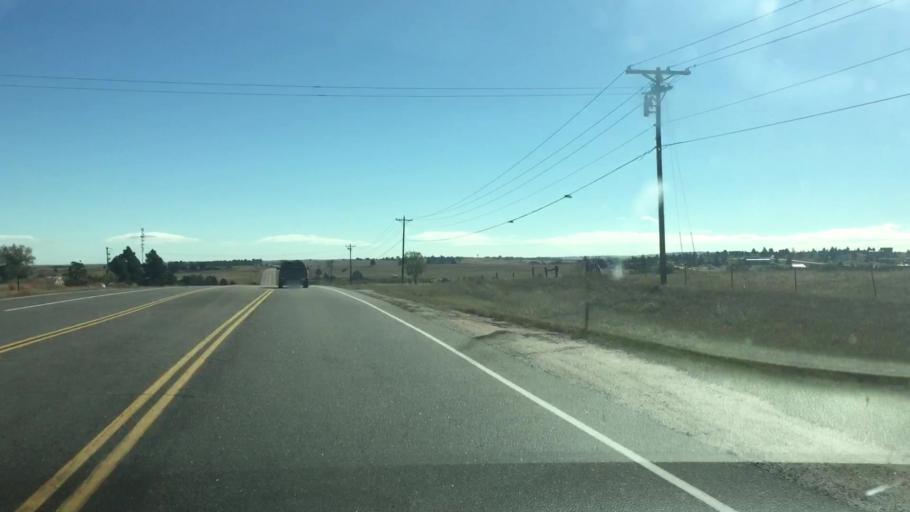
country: US
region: Colorado
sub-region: Elbert County
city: Elizabeth
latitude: 39.3613
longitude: -104.5617
